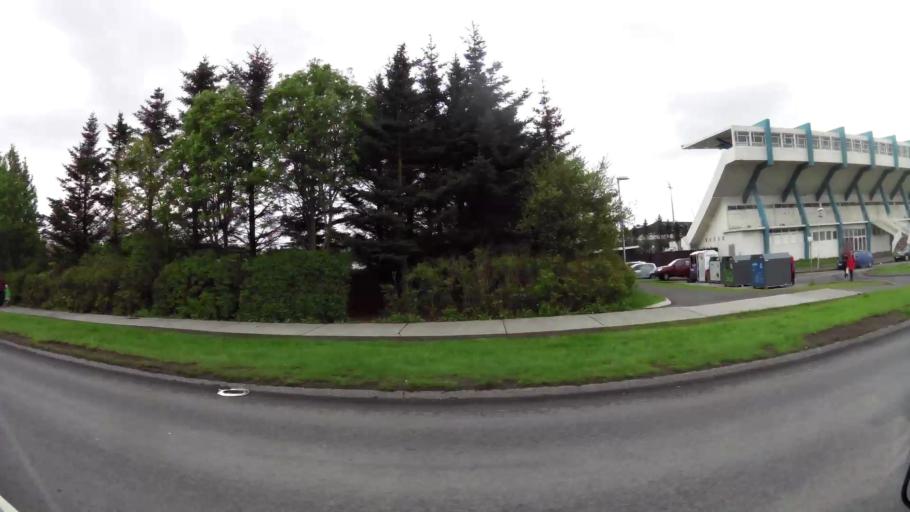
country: IS
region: Capital Region
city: Reykjavik
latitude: 64.1468
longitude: -21.8778
